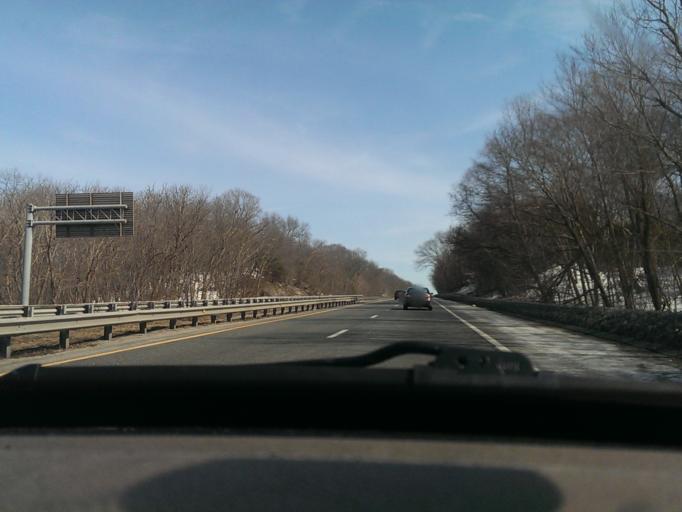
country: US
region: Rhode Island
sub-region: Providence County
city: North Smithfield
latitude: 41.9748
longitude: -71.5289
